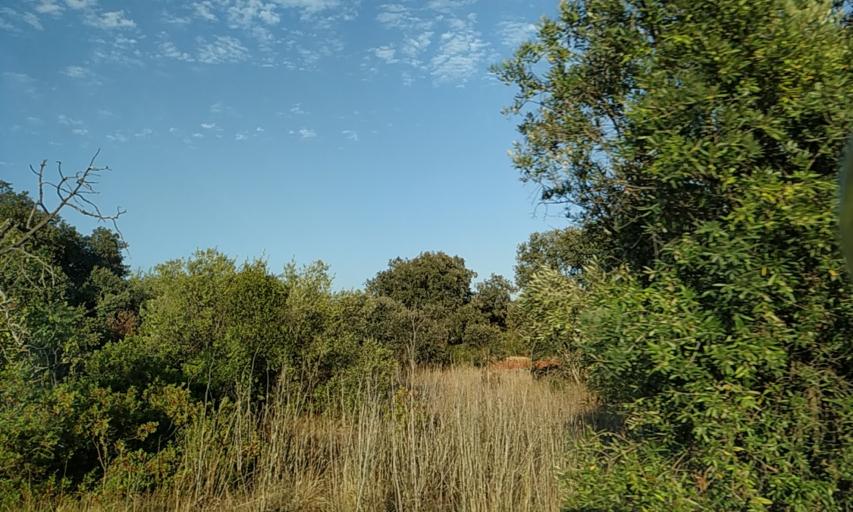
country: PT
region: Santarem
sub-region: Alcanena
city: Alcanena
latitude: 39.4439
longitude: -8.6239
